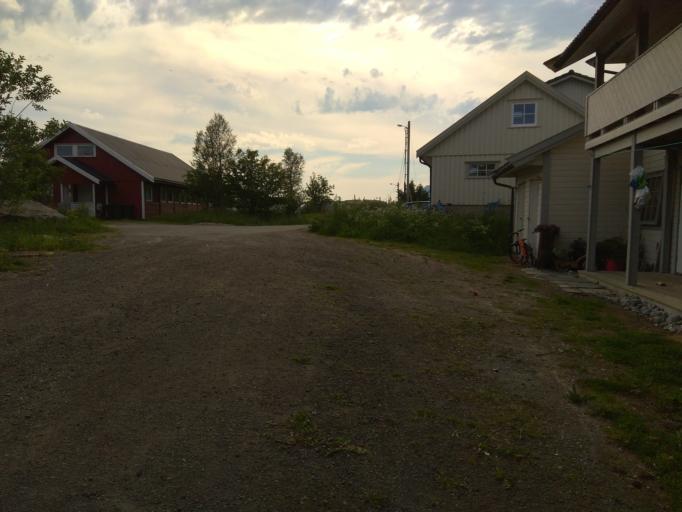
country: NO
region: Nordland
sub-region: Moskenes
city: Reine
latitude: 67.8937
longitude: 13.0256
